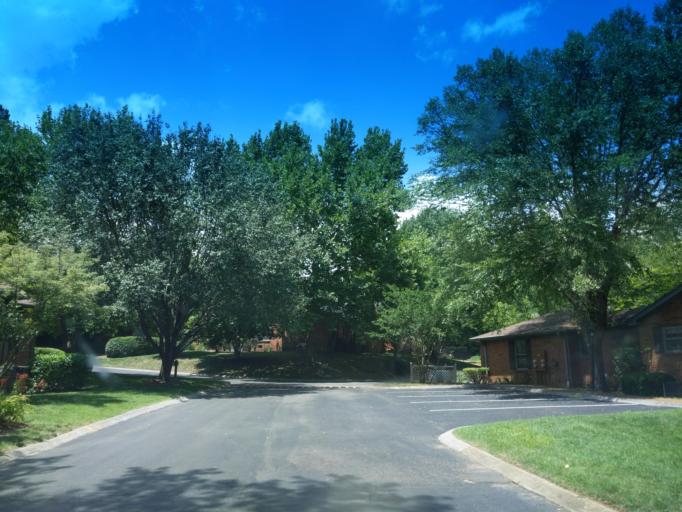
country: US
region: Tennessee
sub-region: Williamson County
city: Brentwood
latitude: 36.0417
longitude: -86.7650
